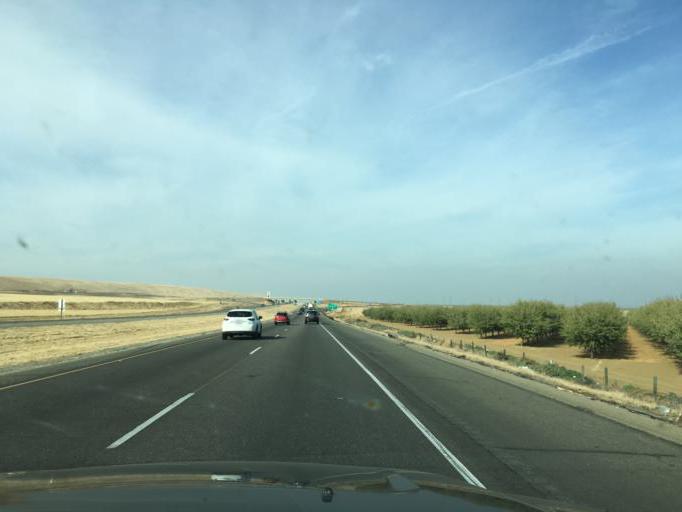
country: US
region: California
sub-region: Merced County
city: South Dos Palos
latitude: 36.8443
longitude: -120.7696
